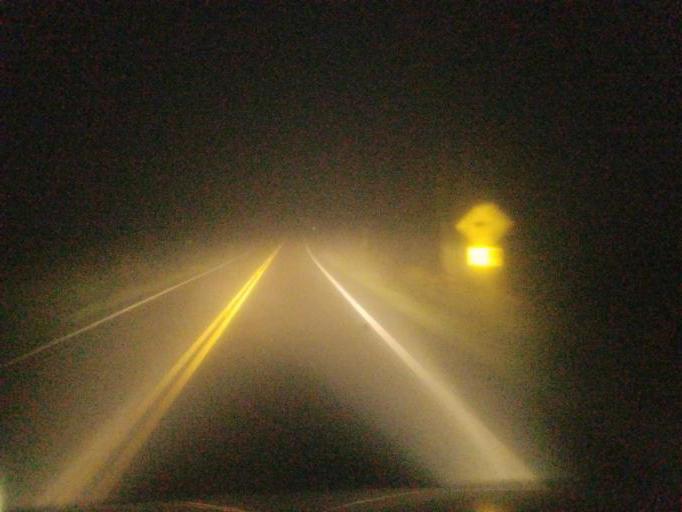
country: US
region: Ohio
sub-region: Knox County
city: Oak Hill
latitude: 40.2840
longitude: -82.1424
